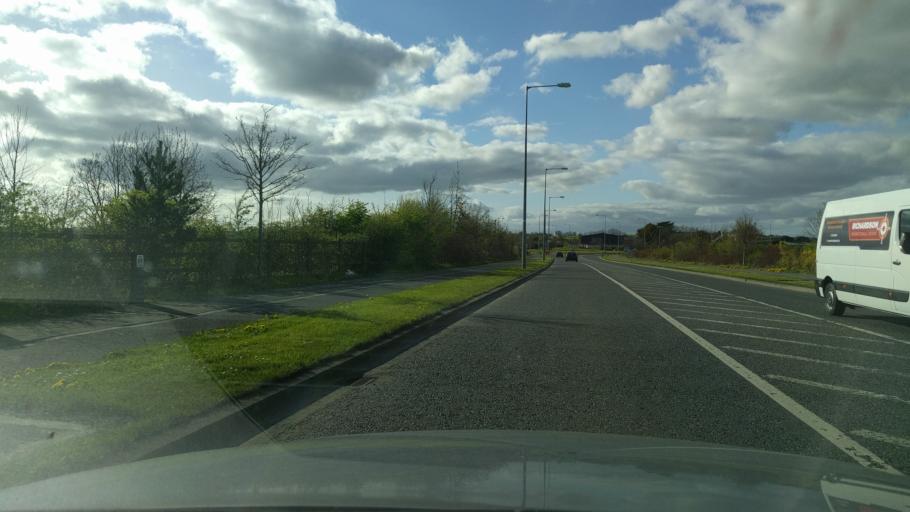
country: IE
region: Leinster
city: Balrothery
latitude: 53.6022
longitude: -6.2063
